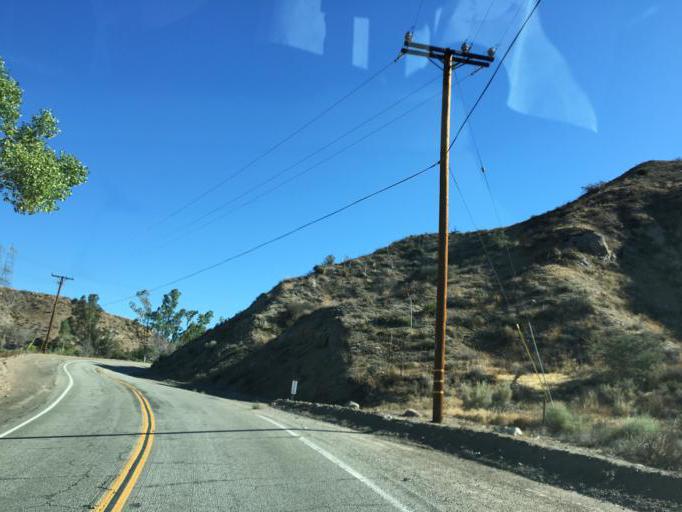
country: US
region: California
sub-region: Los Angeles County
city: Agua Dulce
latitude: 34.4585
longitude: -118.3304
